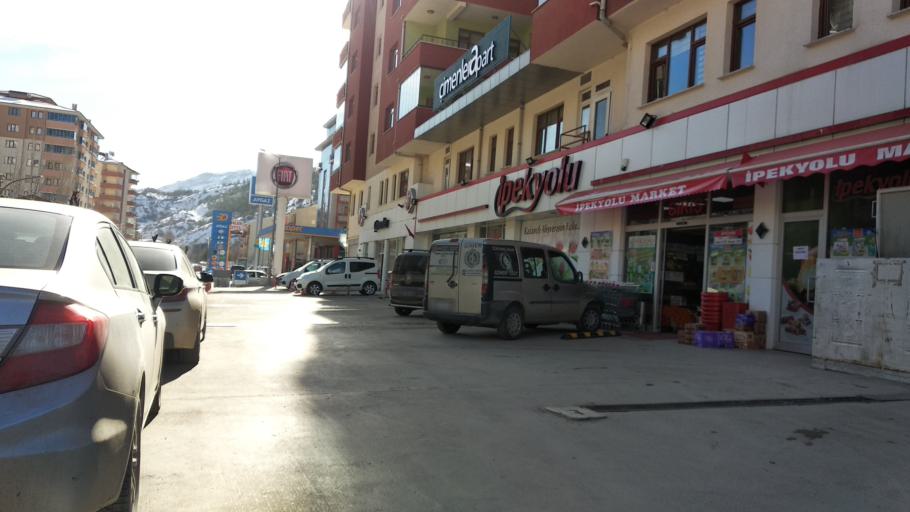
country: TR
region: Gumushane
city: Gumushkhane
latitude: 40.4504
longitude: 39.4952
